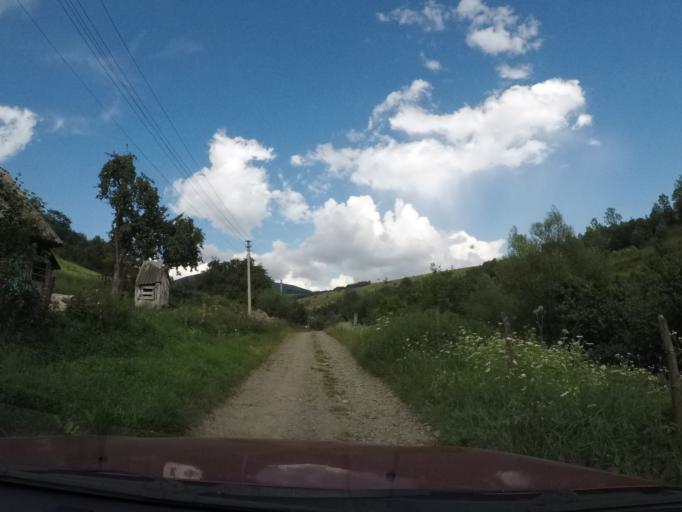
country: UA
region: Zakarpattia
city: Velykyi Bereznyi
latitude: 49.0224
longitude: 22.6350
